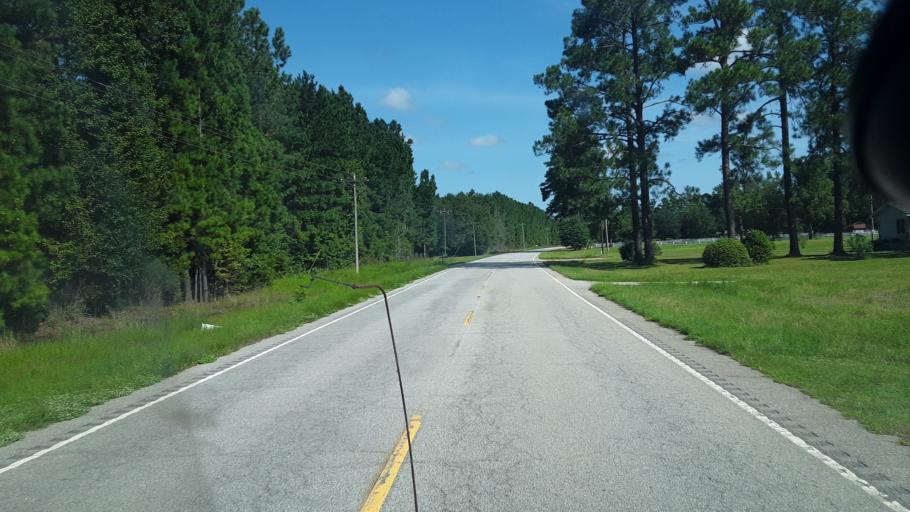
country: US
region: South Carolina
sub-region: Hampton County
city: Varnville
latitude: 32.7664
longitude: -81.0507
